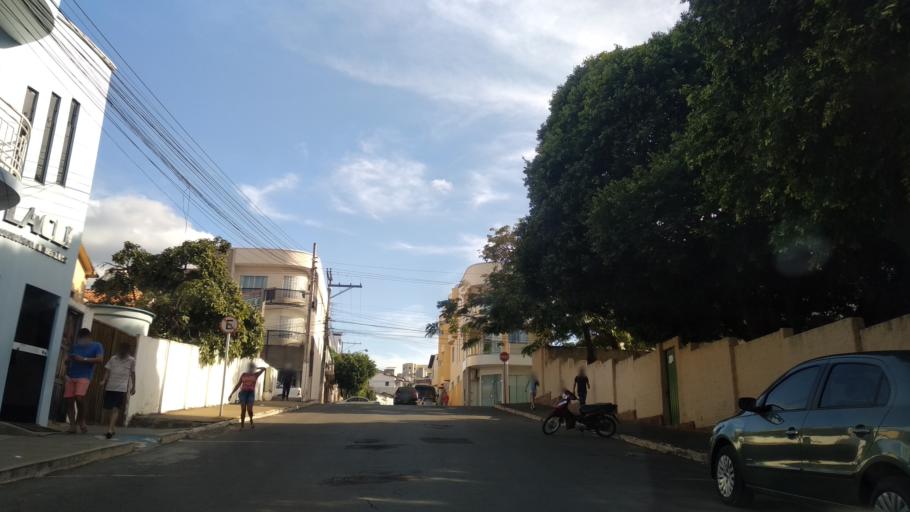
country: BR
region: Bahia
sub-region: Caetite
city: Caetite
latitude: -14.0696
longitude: -42.4898
